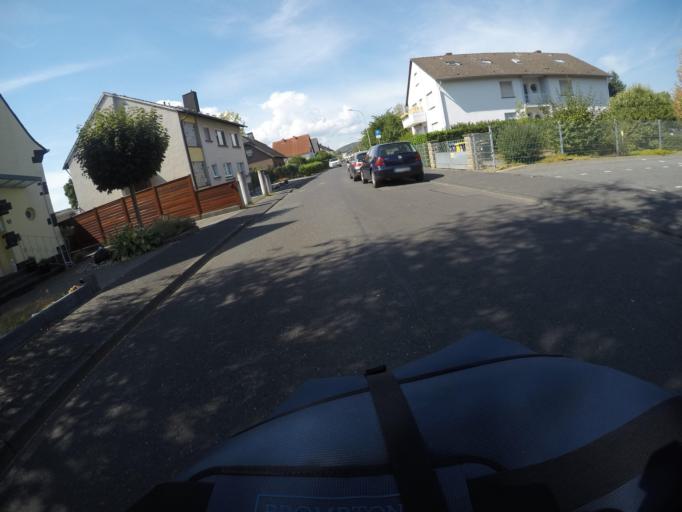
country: DE
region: Rheinland-Pfalz
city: Sinzig
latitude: 50.5486
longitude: 7.2651
